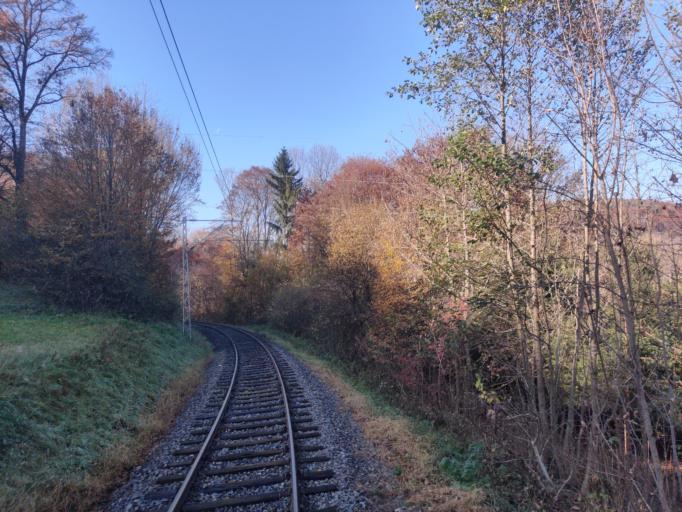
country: AT
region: Styria
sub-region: Politischer Bezirk Suedoststeiermark
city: Maierdorf
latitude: 46.8903
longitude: 15.8585
